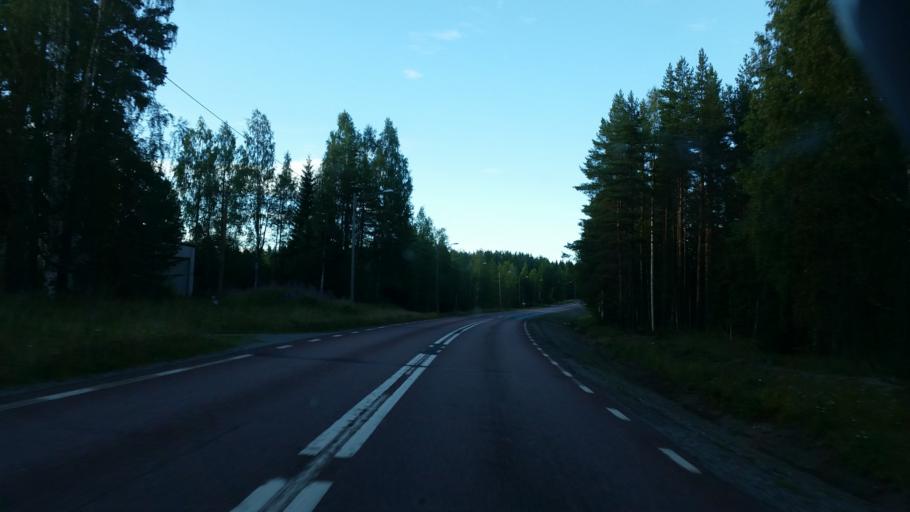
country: SE
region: Vaesterbotten
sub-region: Dorotea Kommun
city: Dorotea
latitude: 64.1593
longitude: 16.2625
